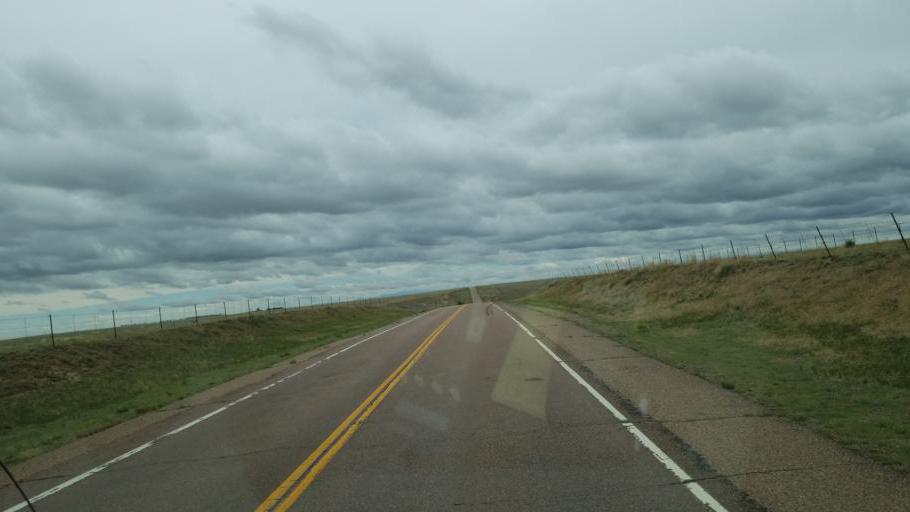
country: US
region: Colorado
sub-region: Lincoln County
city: Limon
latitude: 38.8392
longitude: -103.8989
